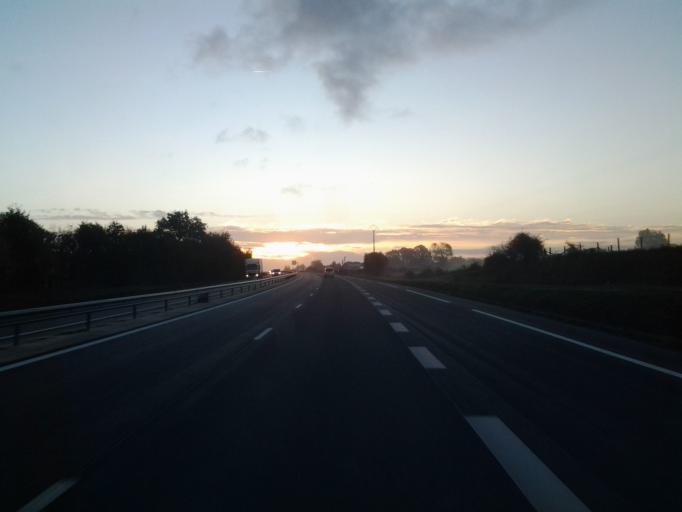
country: FR
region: Pays de la Loire
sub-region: Departement de la Vendee
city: La Chaize-le-Vicomte
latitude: 46.6560
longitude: -1.2400
